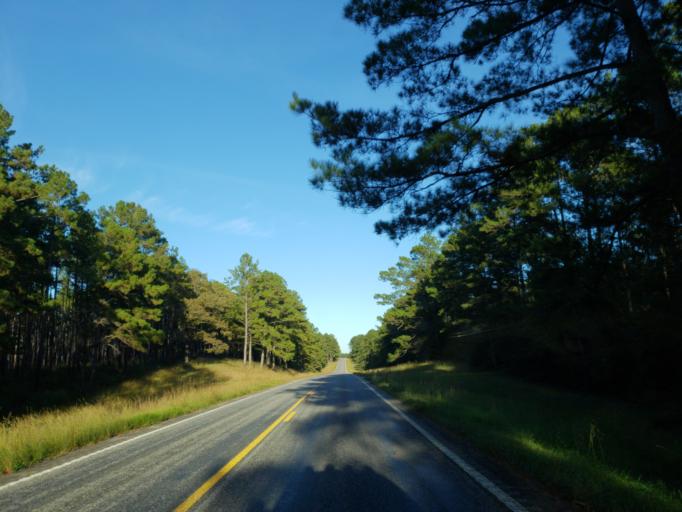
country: US
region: Mississippi
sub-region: Wayne County
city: Belmont
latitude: 31.3999
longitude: -88.6350
